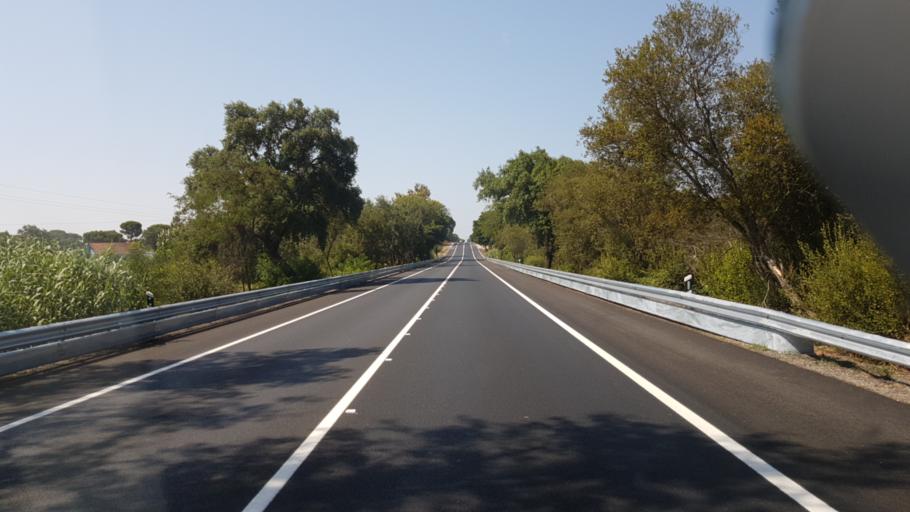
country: PT
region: Setubal
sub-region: Grandola
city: Grandola
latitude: 38.2365
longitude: -8.5524
